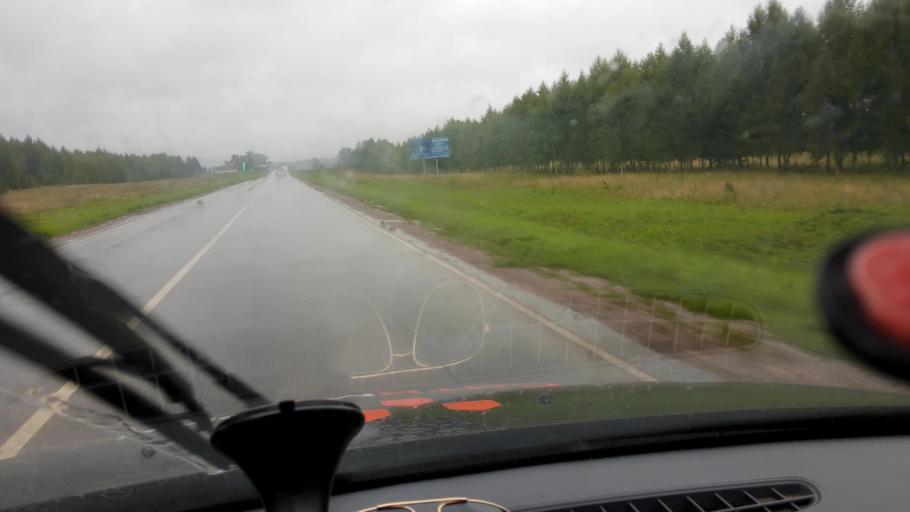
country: RU
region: Bashkortostan
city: Karmaskaly
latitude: 53.9180
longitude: 56.4342
